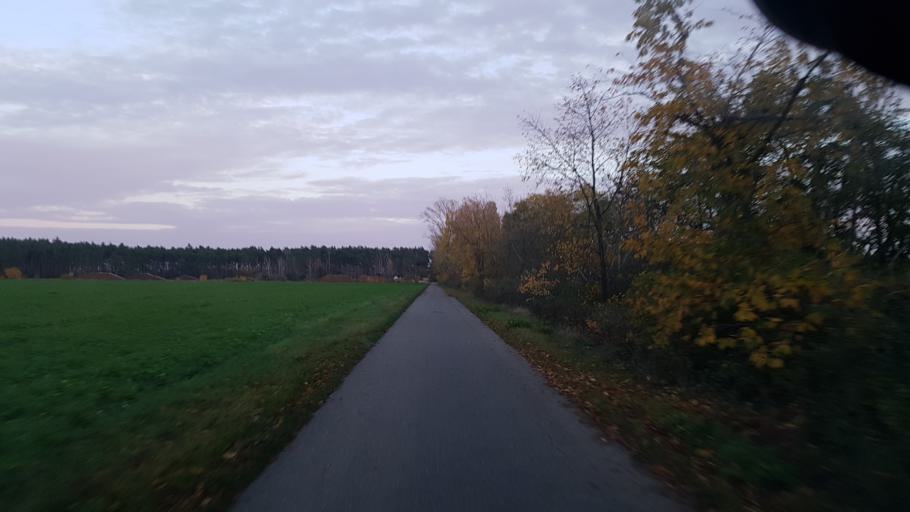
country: DE
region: Brandenburg
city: Bad Liebenwerda
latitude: 51.5114
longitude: 13.3115
